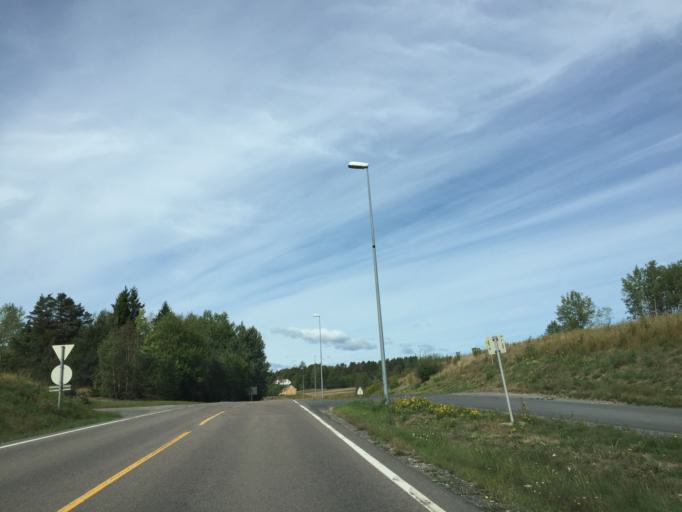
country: NO
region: Akershus
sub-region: Vestby
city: Vestby
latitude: 59.5175
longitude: 10.7202
